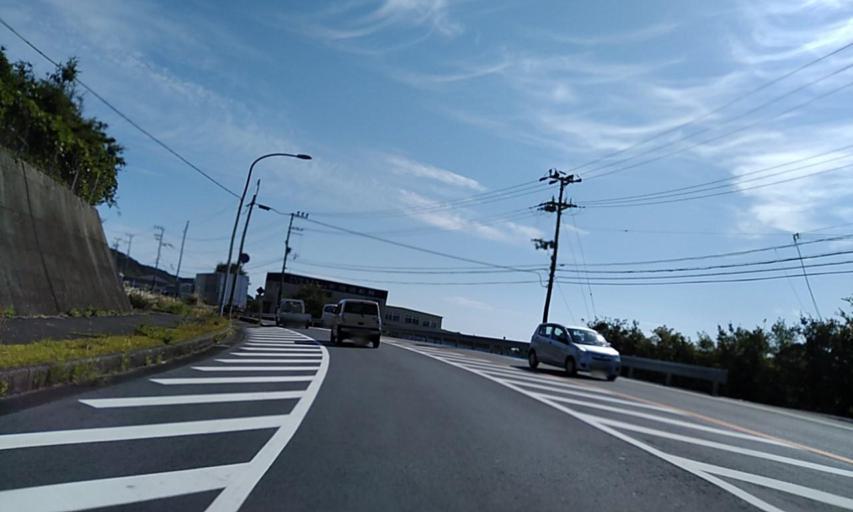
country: JP
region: Wakayama
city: Gobo
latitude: 33.8586
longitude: 135.1608
